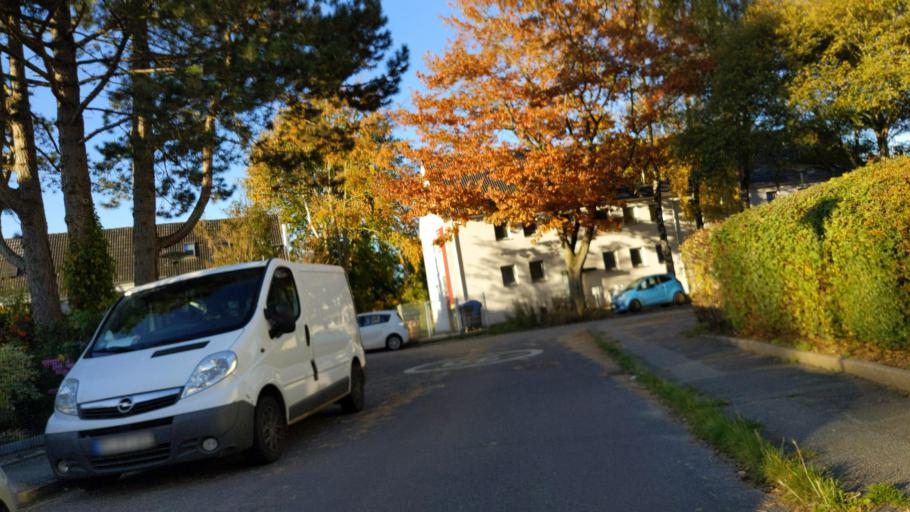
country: DE
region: Schleswig-Holstein
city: Gross Gronau
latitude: 53.8461
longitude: 10.7386
